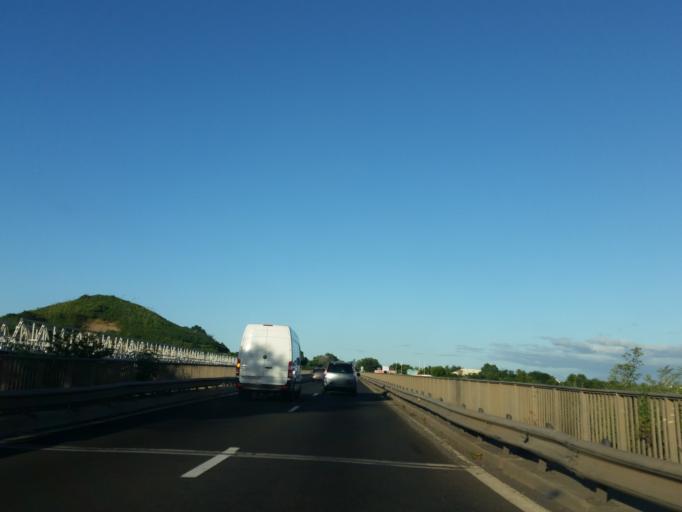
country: RE
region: Reunion
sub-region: Reunion
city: Le Port
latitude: -20.9578
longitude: 55.3091
